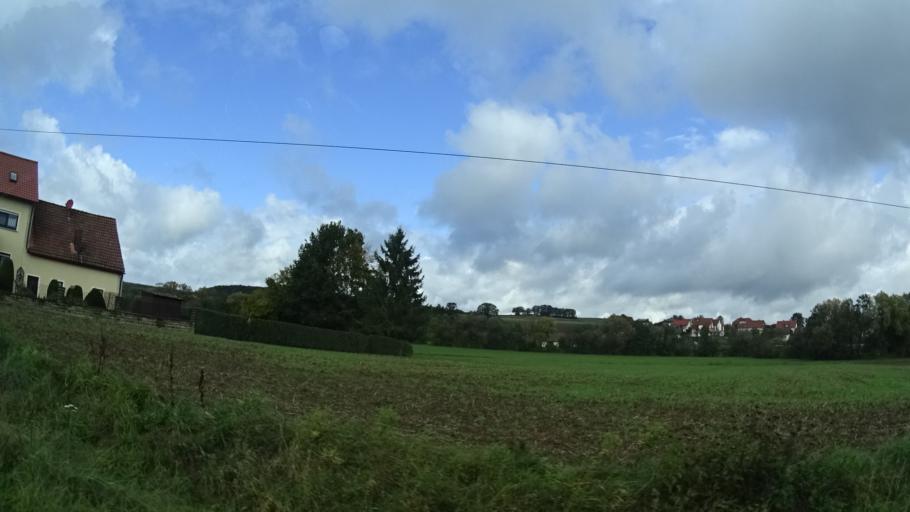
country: DE
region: Bavaria
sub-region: Upper Franconia
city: Burgwindheim
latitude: 49.8741
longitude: 10.6198
